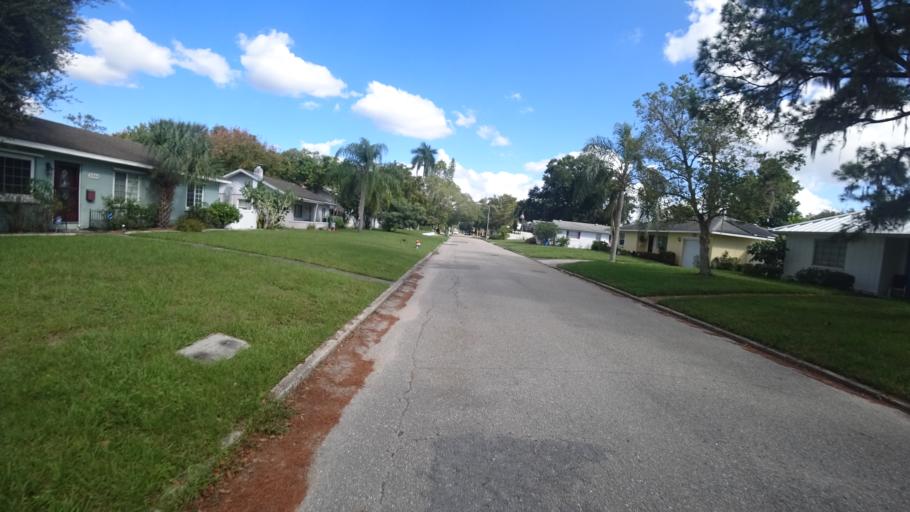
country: US
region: Florida
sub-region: Manatee County
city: Bradenton
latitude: 27.4873
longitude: -82.5849
